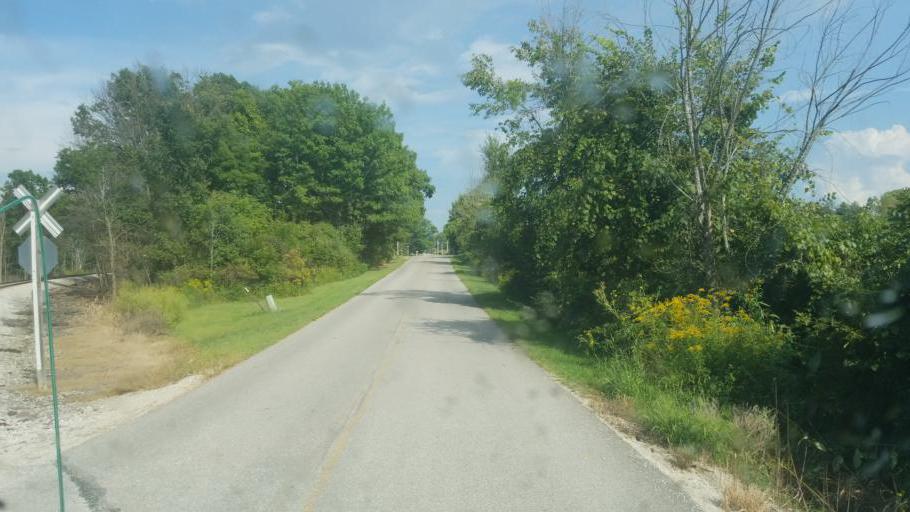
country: US
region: Ohio
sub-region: Huron County
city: Plymouth
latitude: 41.0068
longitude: -82.6245
